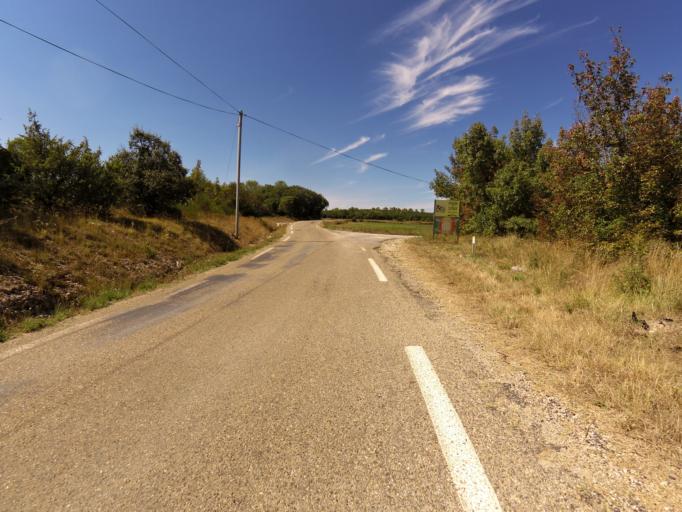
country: FR
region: Languedoc-Roussillon
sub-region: Departement du Gard
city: Sommieres
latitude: 43.8450
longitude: 4.0556
